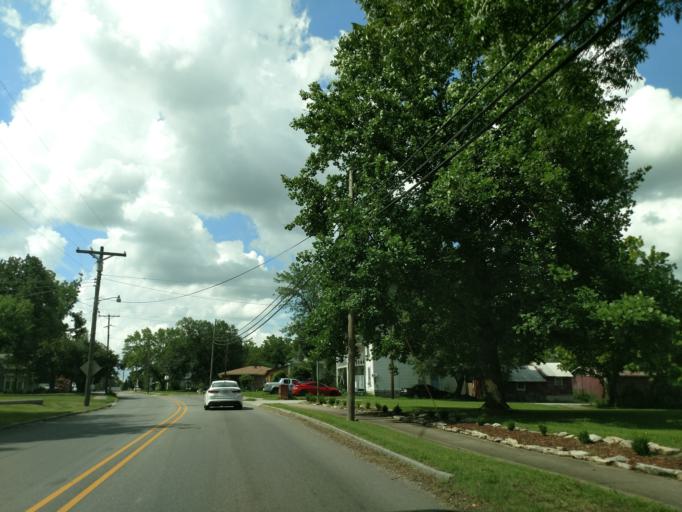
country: US
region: Arkansas
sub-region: Carroll County
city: Berryville
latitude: 36.3623
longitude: -93.5644
